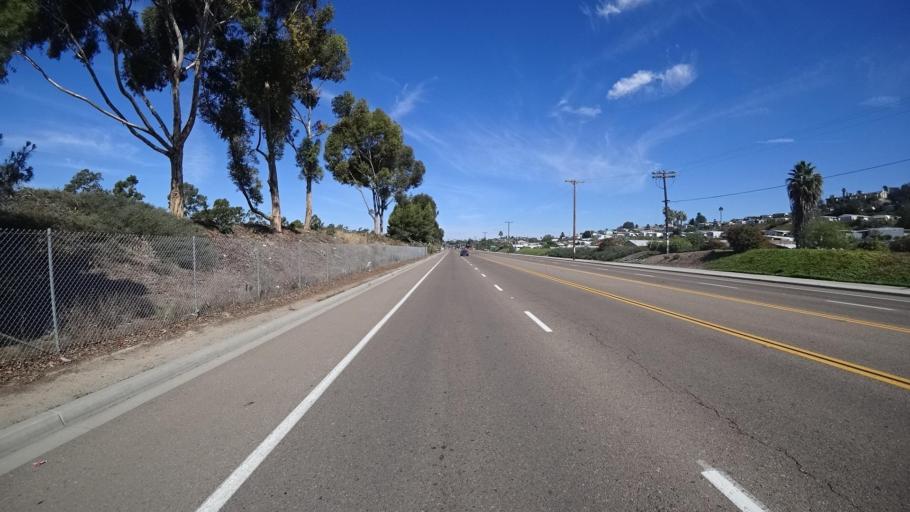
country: US
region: California
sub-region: San Diego County
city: La Presa
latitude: 32.7217
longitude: -117.0142
